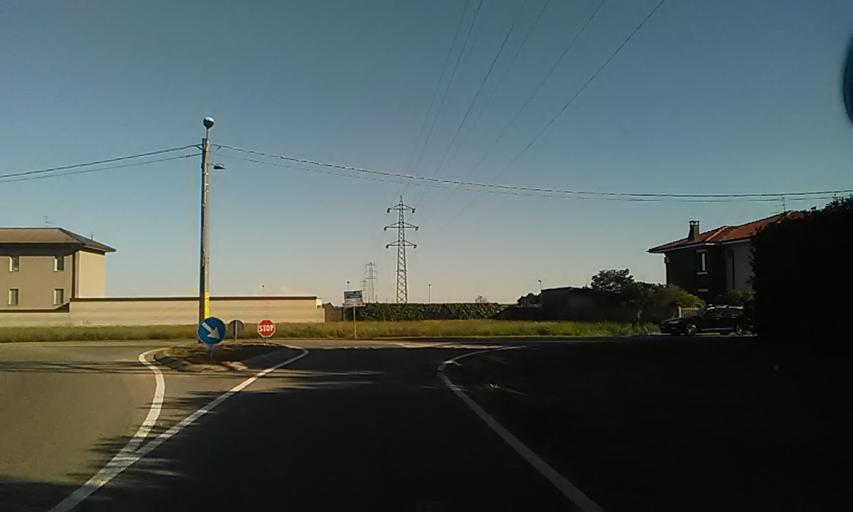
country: IT
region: Piedmont
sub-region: Provincia di Novara
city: Momo
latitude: 45.5764
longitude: 8.5613
